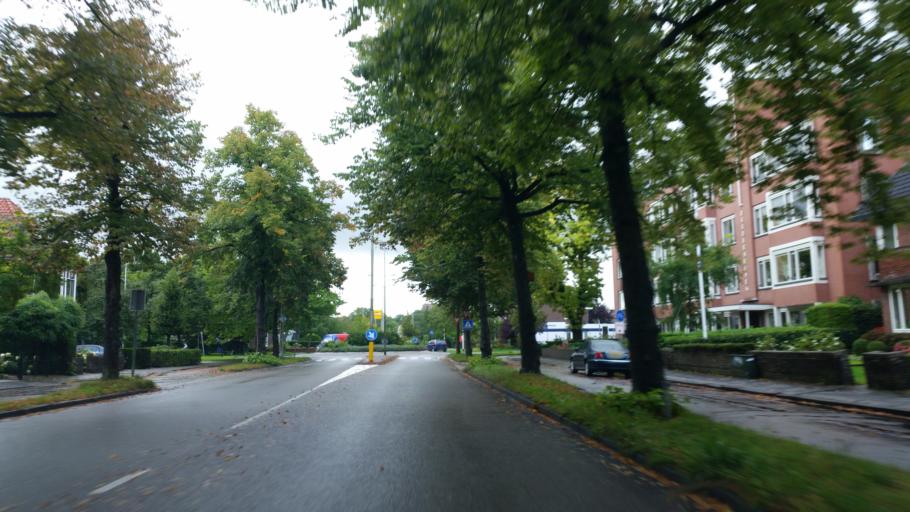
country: NL
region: Friesland
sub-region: Gemeente Leeuwarden
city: Bilgaard
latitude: 53.2089
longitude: 5.7847
